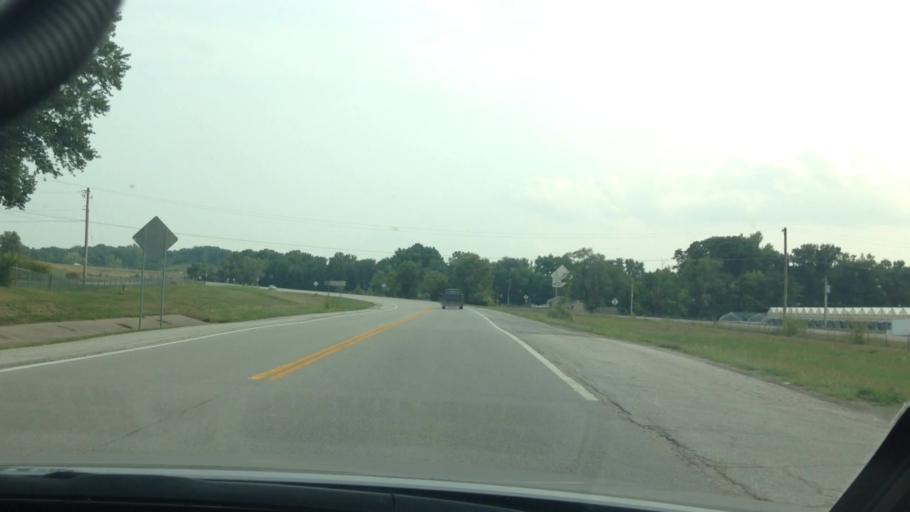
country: US
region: Kansas
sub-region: Leavenworth County
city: Lansing
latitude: 39.1856
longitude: -94.8030
